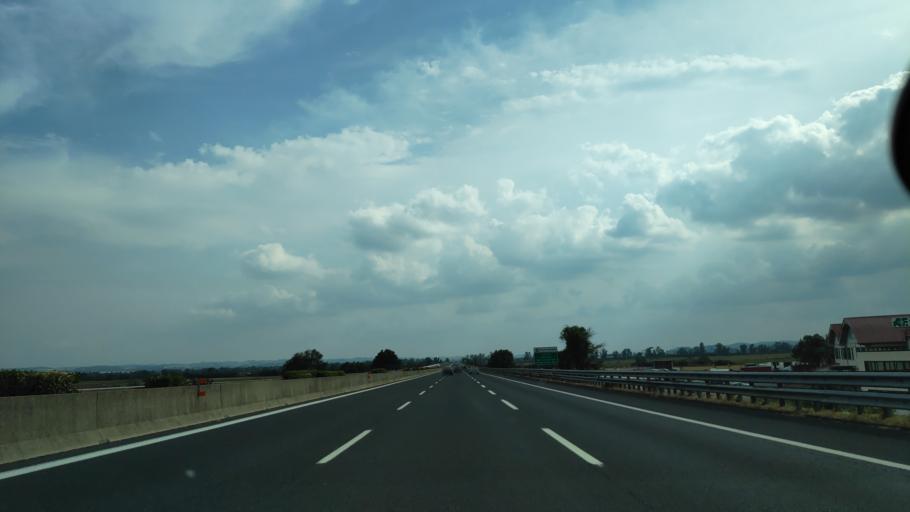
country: IT
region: Latium
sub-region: Citta metropolitana di Roma Capitale
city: Fiano Romano
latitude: 42.1455
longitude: 12.6228
